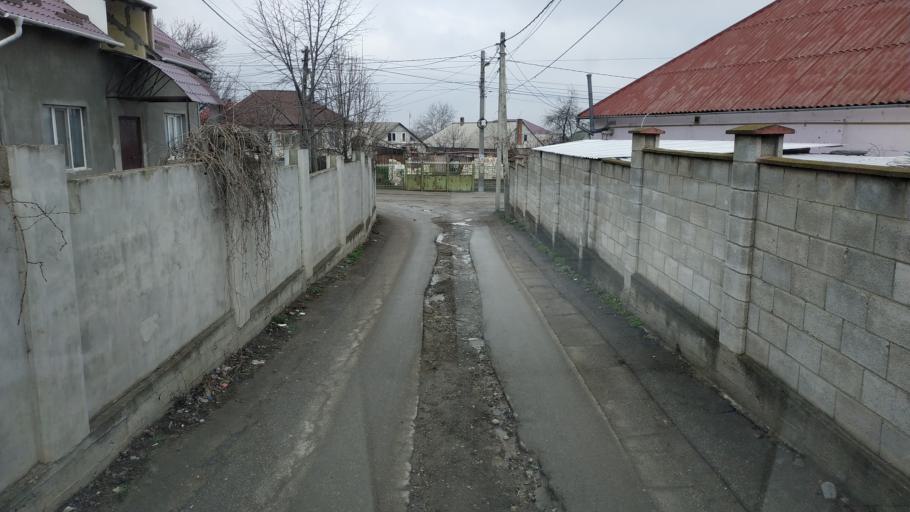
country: MD
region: Chisinau
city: Vatra
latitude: 47.0180
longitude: 28.7564
